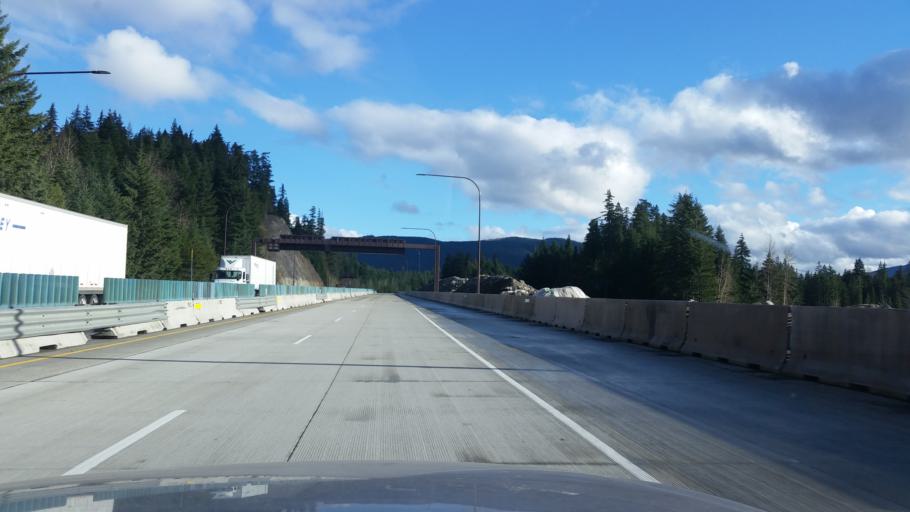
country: US
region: Washington
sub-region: Kittitas County
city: Cle Elum
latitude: 47.3293
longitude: -121.3402
